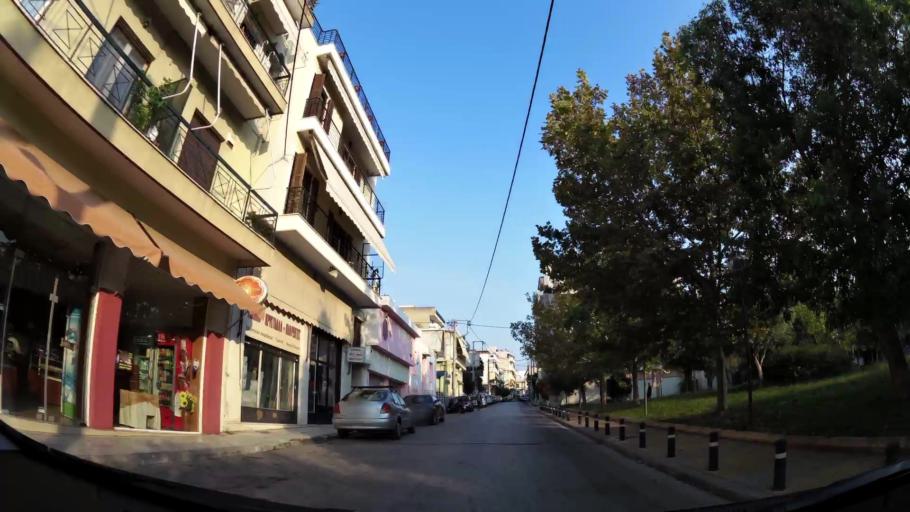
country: GR
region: Attica
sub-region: Nomarchia Athinas
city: Nea Filadelfeia
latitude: 38.0283
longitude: 23.7444
